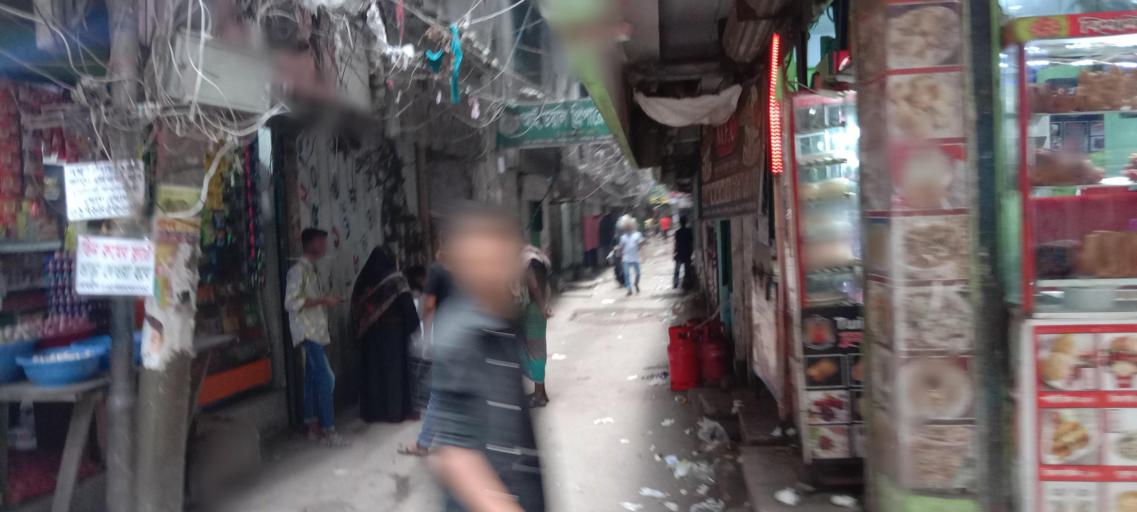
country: BD
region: Dhaka
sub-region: Dhaka
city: Dhaka
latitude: 23.7015
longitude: 90.4085
